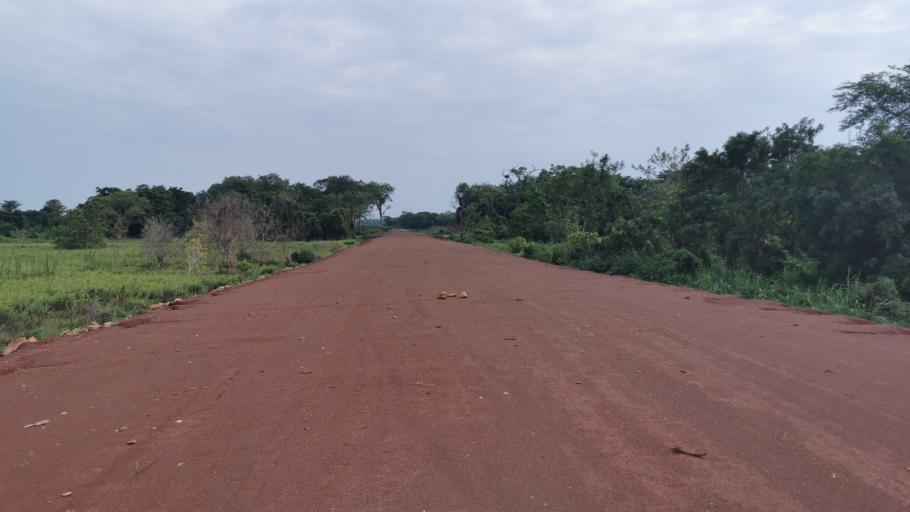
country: ET
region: Gambela
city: Gambela
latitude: 7.8715
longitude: 34.4955
